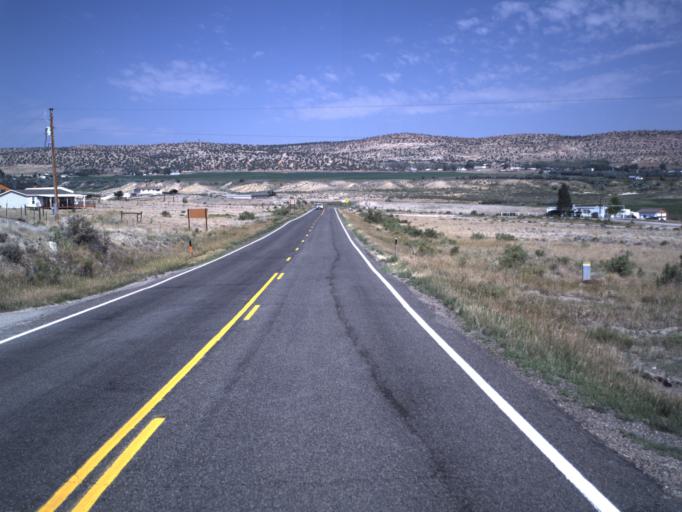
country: US
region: Utah
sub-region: Daggett County
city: Manila
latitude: 40.9717
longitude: -109.7171
